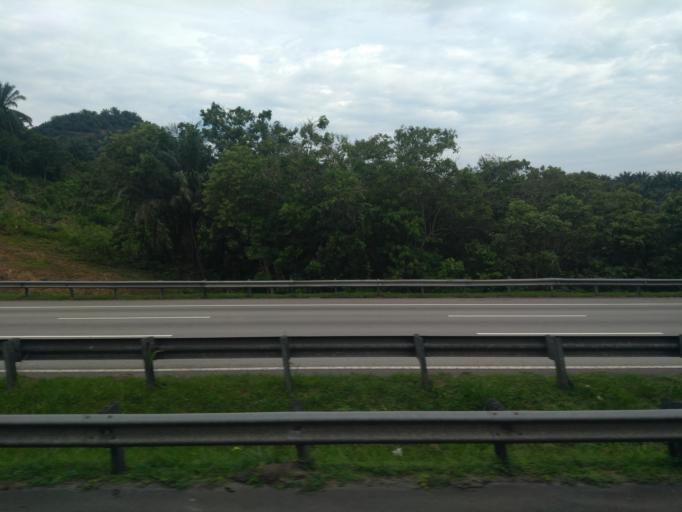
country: MY
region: Negeri Sembilan
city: Tampin
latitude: 2.4667
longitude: 102.1501
